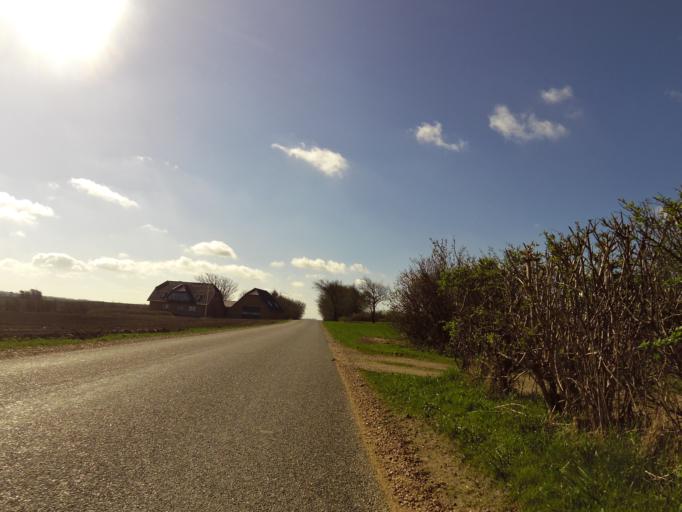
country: DK
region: Central Jutland
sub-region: Holstebro Kommune
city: Vinderup
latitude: 56.4573
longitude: 8.7221
